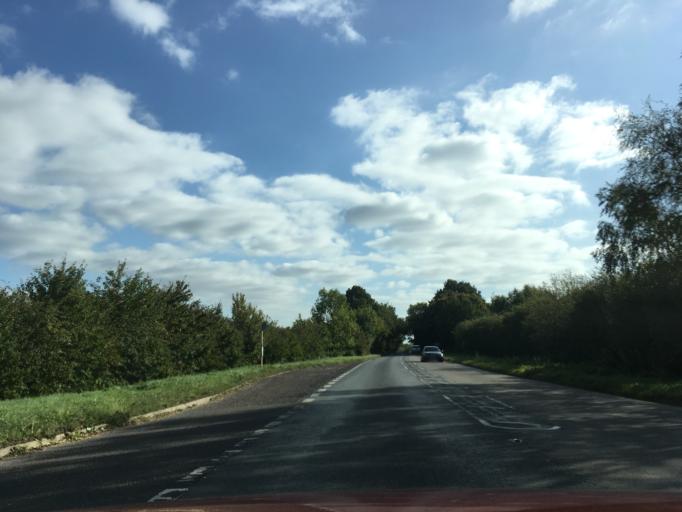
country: GB
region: England
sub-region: Hampshire
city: Tadley
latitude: 51.3082
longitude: -1.1150
